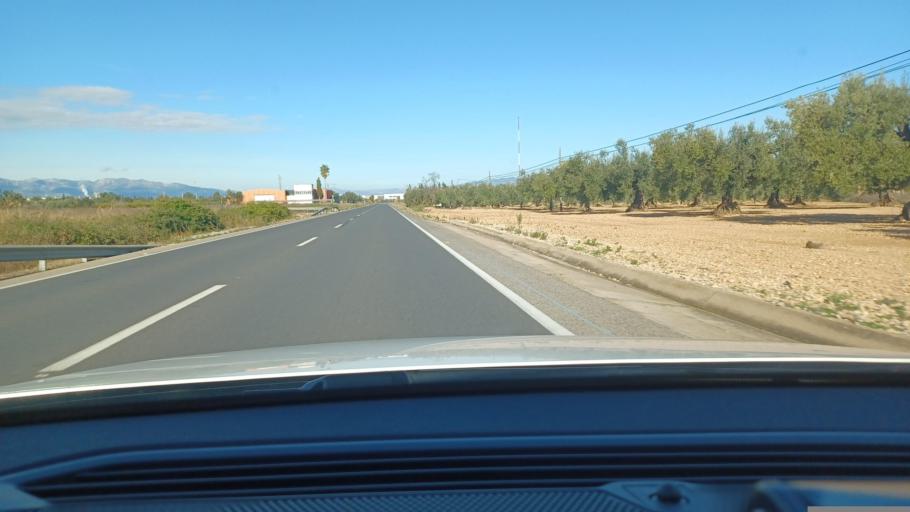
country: ES
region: Catalonia
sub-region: Provincia de Tarragona
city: Santa Barbara
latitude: 40.7295
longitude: 0.5033
